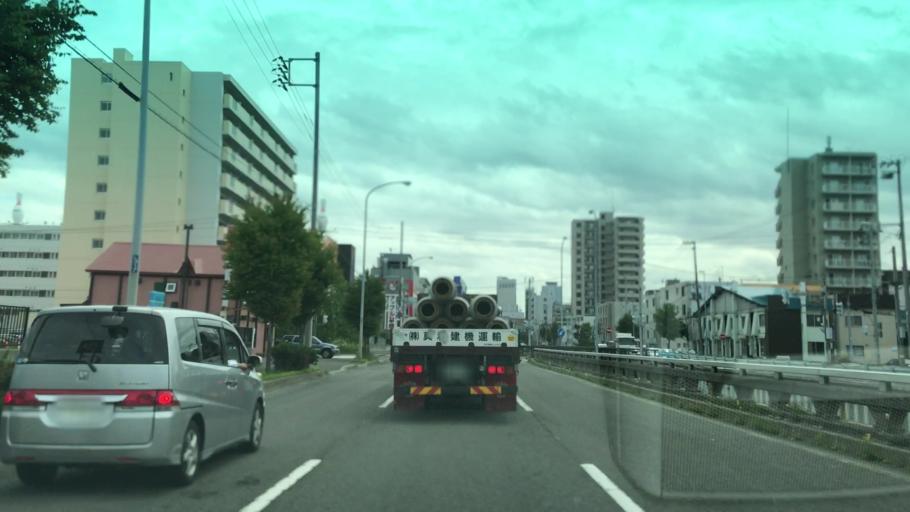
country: JP
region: Hokkaido
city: Sapporo
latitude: 43.0885
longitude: 141.3484
